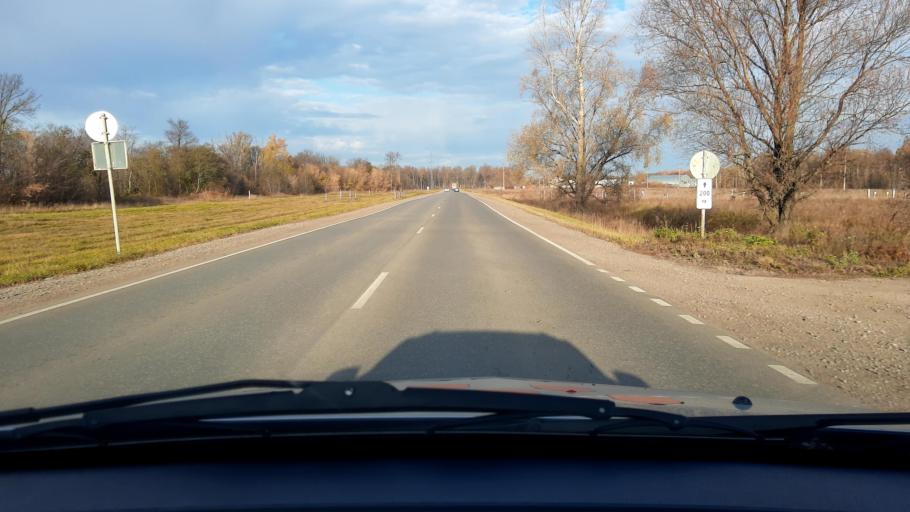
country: RU
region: Bashkortostan
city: Mikhaylovka
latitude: 54.8019
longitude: 55.8321
